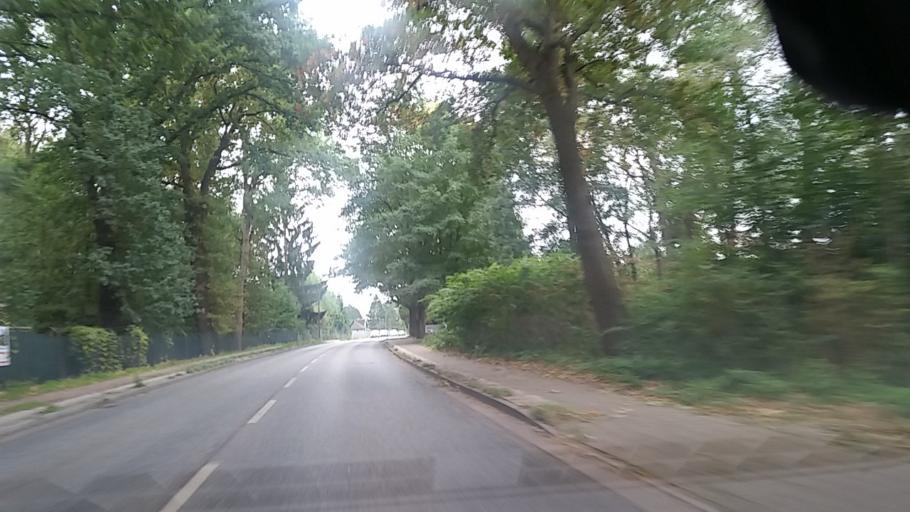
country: DE
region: Hamburg
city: Hummelsbuettel
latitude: 53.6534
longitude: 10.0439
